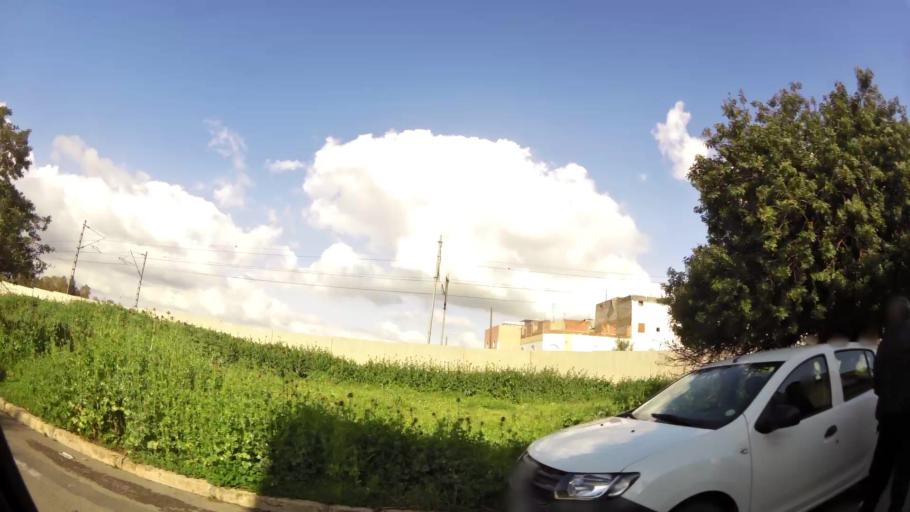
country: MA
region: Chaouia-Ouardigha
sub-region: Settat Province
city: Settat
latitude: 33.0112
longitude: -7.6278
